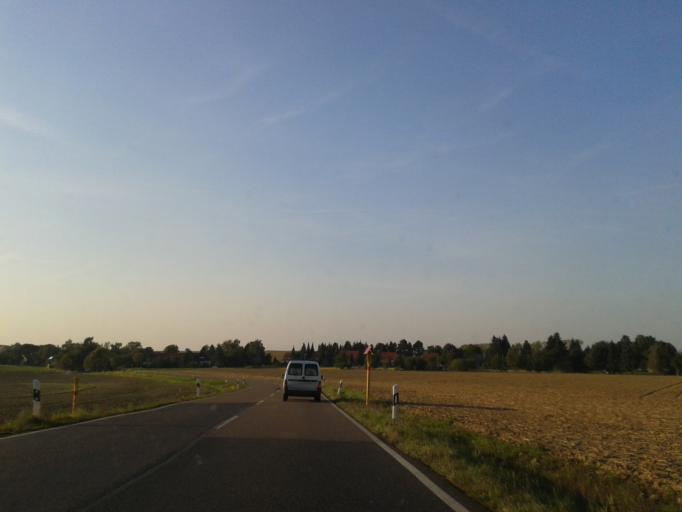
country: DE
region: Saxony
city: Klipphausen
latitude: 51.0739
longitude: 13.5104
